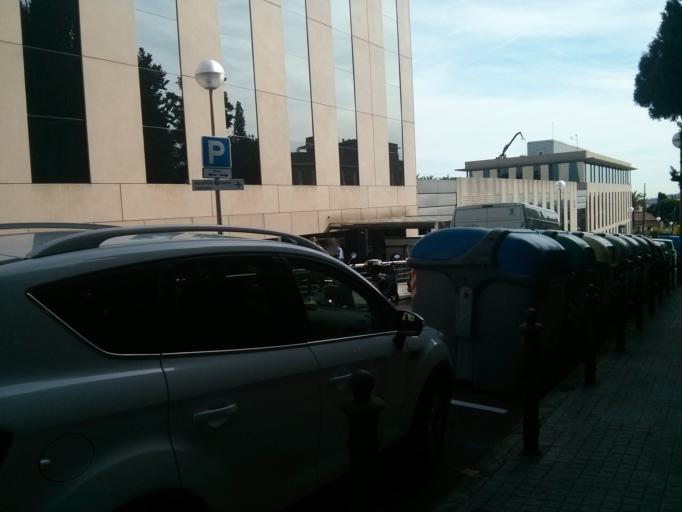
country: ES
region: Catalonia
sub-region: Provincia de Barcelona
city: Sarria-Sant Gervasi
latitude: 41.4067
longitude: 2.1261
